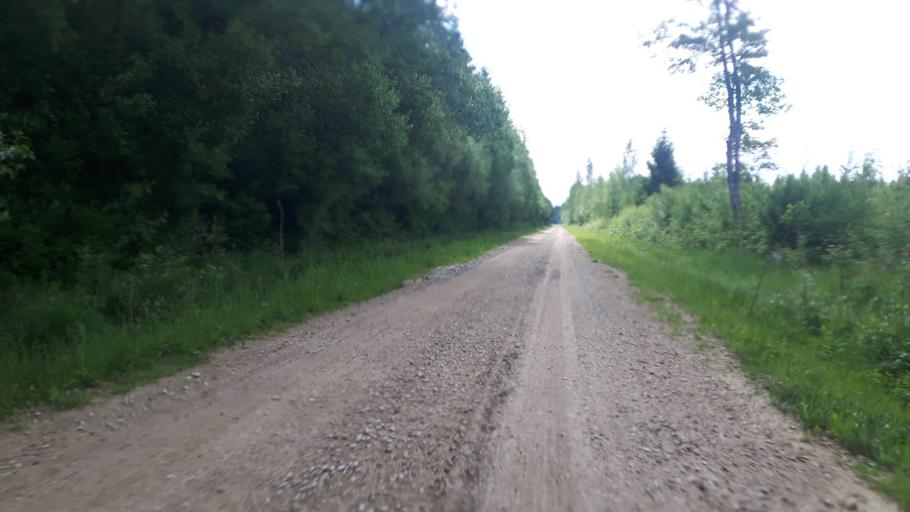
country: EE
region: Paernumaa
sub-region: Vaendra vald (alev)
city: Vandra
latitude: 58.7347
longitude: 25.0009
